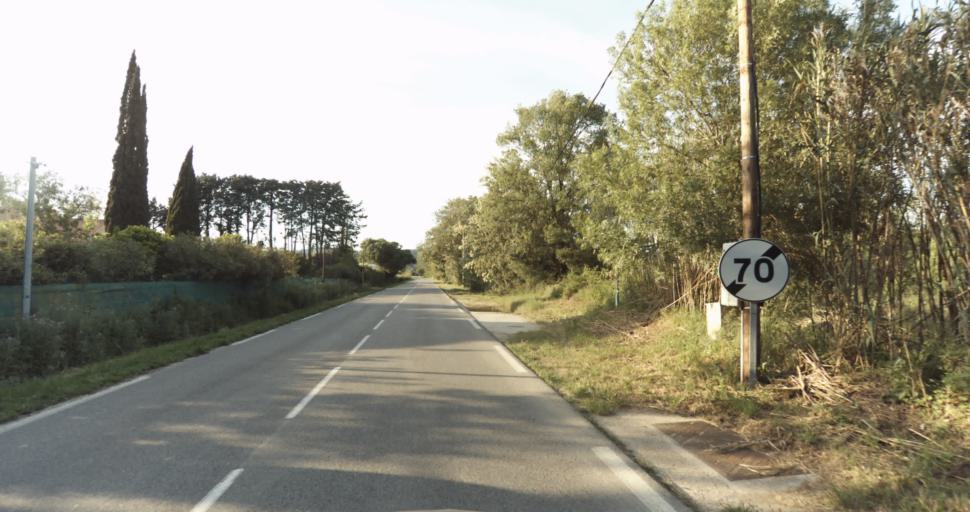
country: FR
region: Provence-Alpes-Cote d'Azur
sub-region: Departement du Var
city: Hyeres
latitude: 43.1366
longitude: 6.1573
